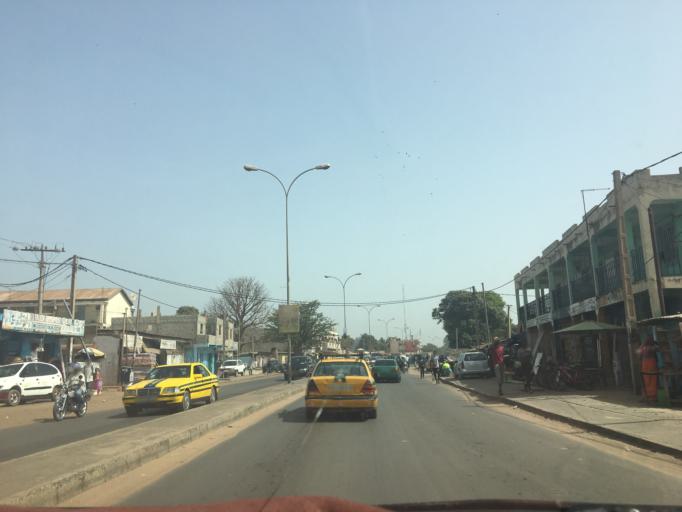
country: GM
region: Western
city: Abuko
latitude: 13.4368
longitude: -16.6765
